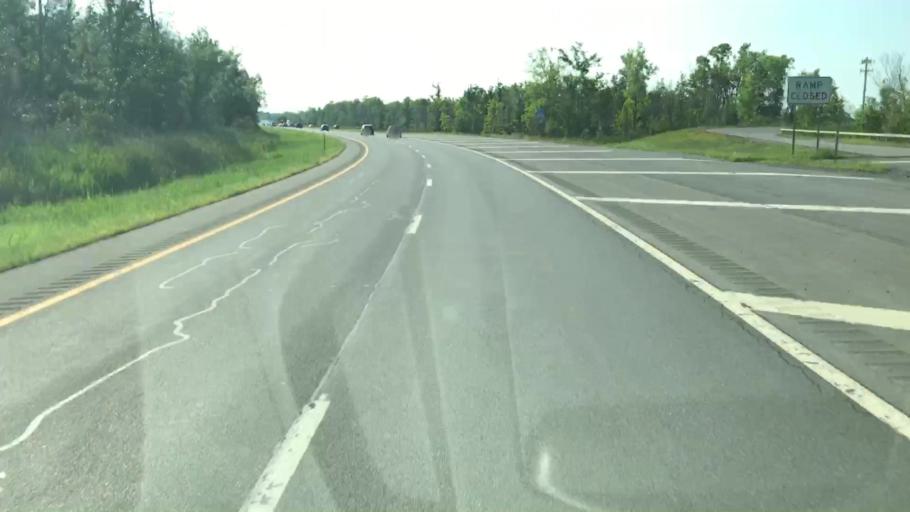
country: US
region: New York
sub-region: Onondaga County
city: East Syracuse
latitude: 43.0563
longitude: -76.0545
